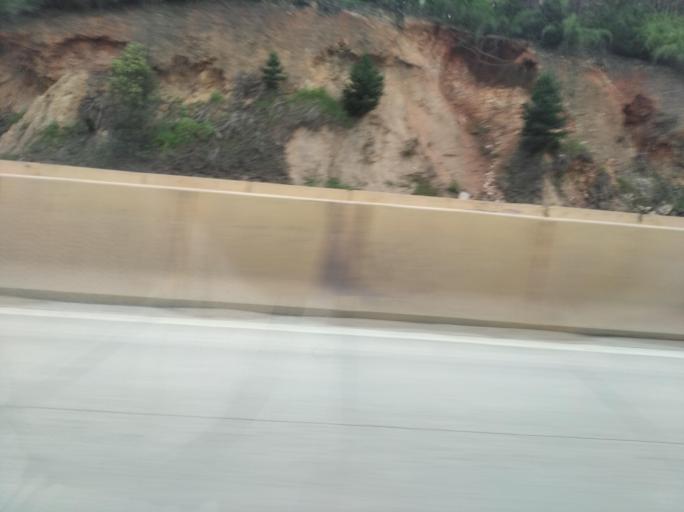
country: CL
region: Valparaiso
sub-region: Provincia de Valparaiso
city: Vina del Mar
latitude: -33.1009
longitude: -71.5729
